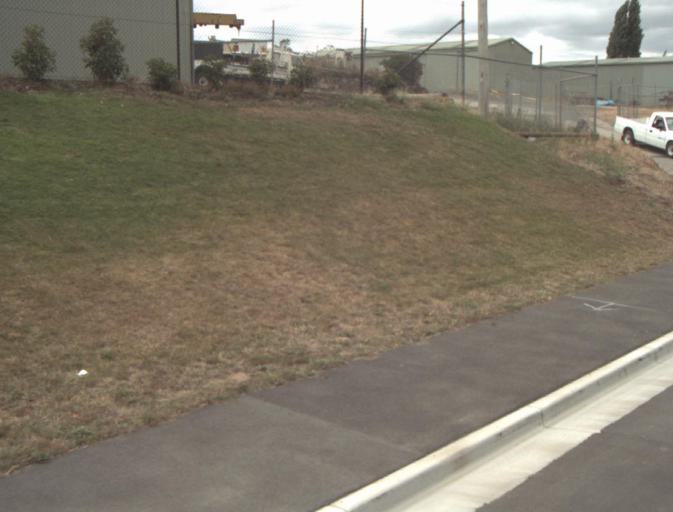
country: AU
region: Tasmania
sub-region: Launceston
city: Newstead
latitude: -41.4423
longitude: 147.1813
